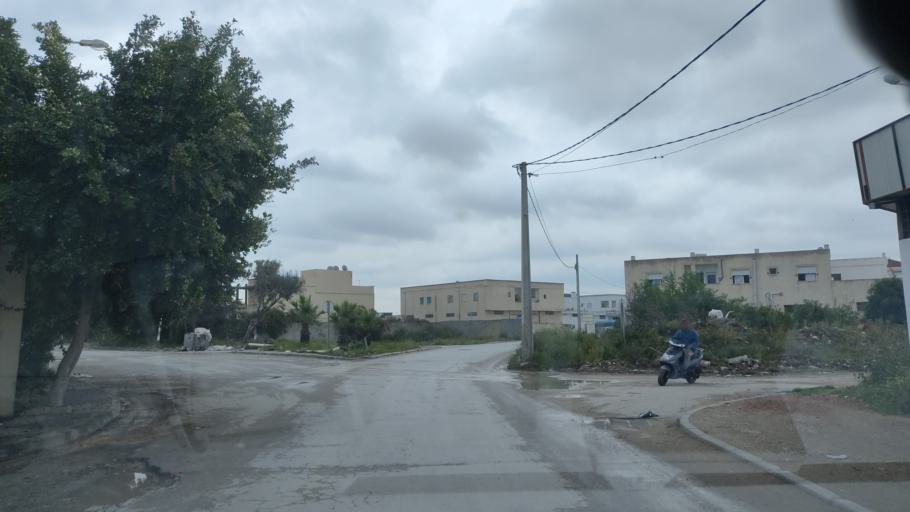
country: TN
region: Ariana
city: Ariana
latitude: 36.8817
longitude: 10.2190
